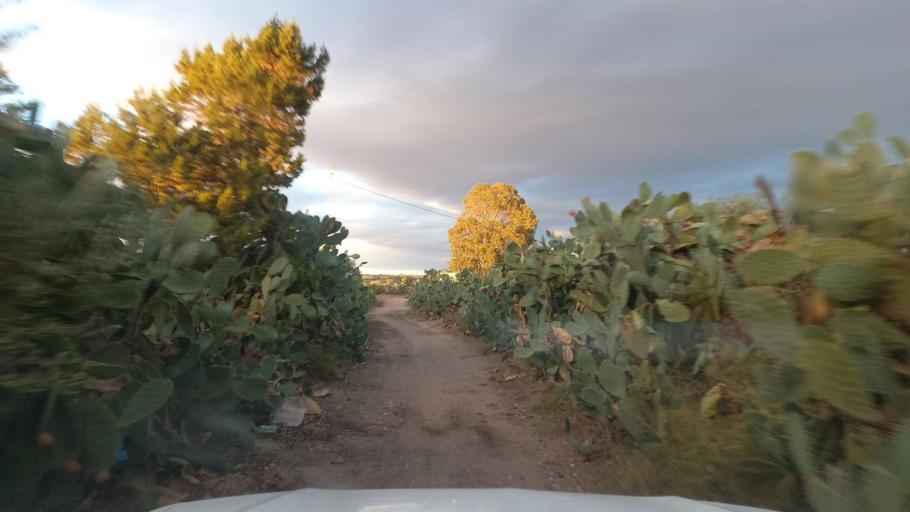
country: TN
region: Al Qasrayn
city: Kasserine
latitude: 35.2601
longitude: 8.9431
